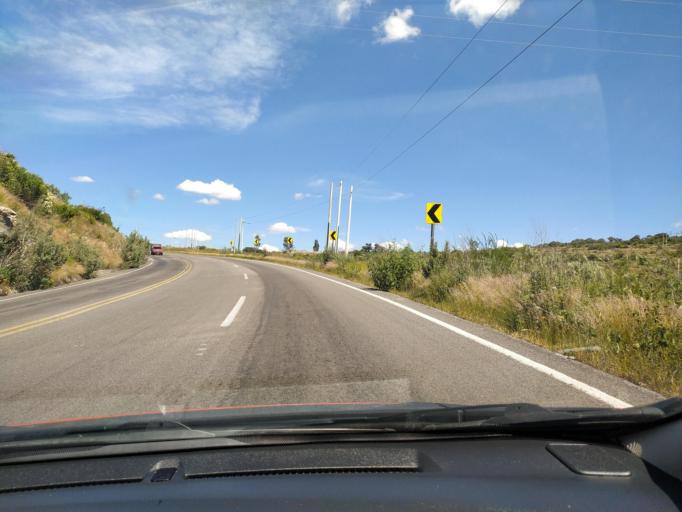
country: MX
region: Jalisco
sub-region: San Julian
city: Colonia Veintitres de Mayo
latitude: 21.0055
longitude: -102.2718
